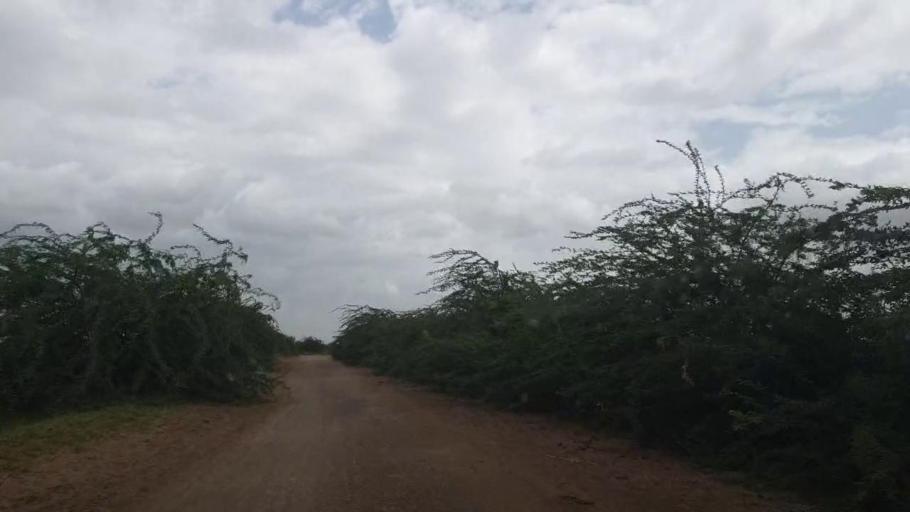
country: PK
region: Sindh
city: Badin
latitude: 24.6441
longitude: 68.9463
